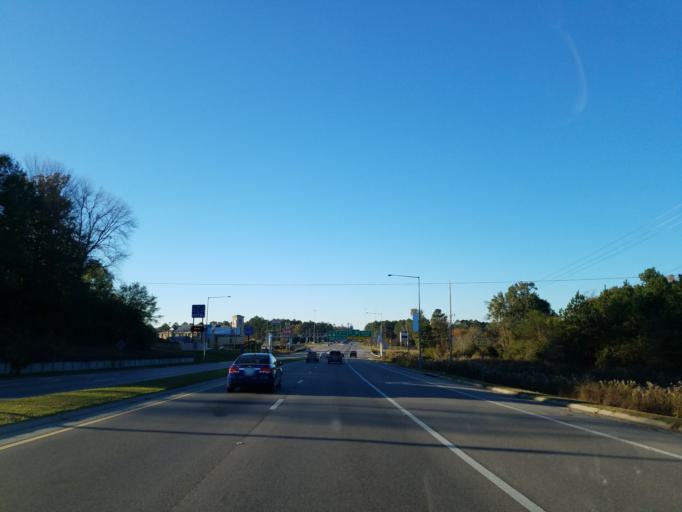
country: US
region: Mississippi
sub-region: Lamar County
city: Arnold Line
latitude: 31.3518
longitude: -89.3406
